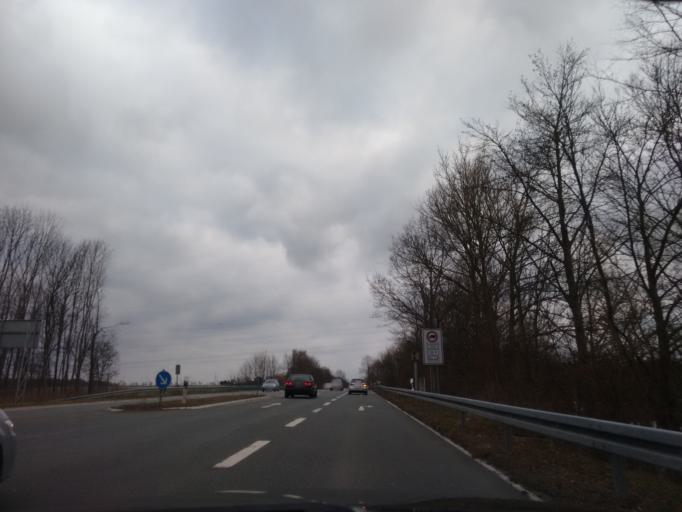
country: DE
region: North Rhine-Westphalia
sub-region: Regierungsbezirk Detmold
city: Paderborn
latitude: 51.7033
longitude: 8.7799
